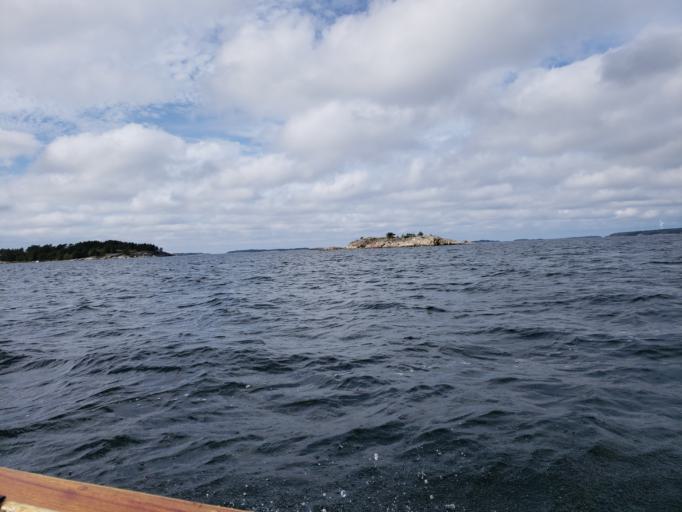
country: FI
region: Varsinais-Suomi
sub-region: Aboland-Turunmaa
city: Dragsfjaerd
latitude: 59.9009
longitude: 22.3453
